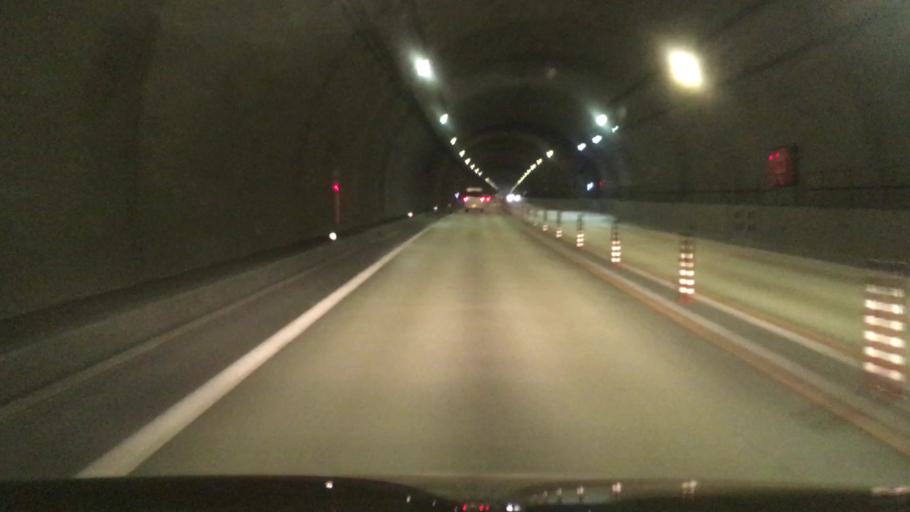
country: JP
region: Hyogo
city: Toyooka
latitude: 35.3708
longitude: 134.7565
